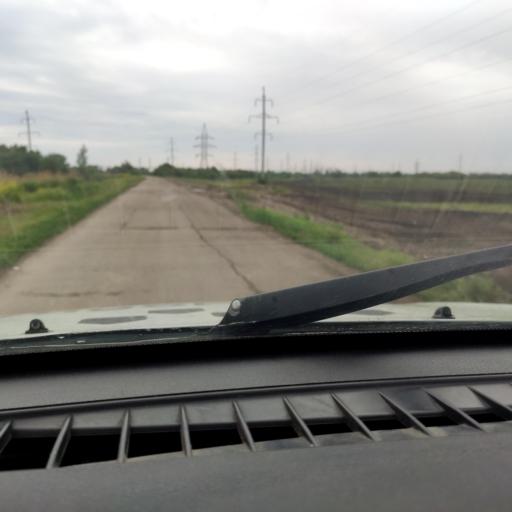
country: RU
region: Samara
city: Tol'yatti
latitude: 53.5919
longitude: 49.4353
